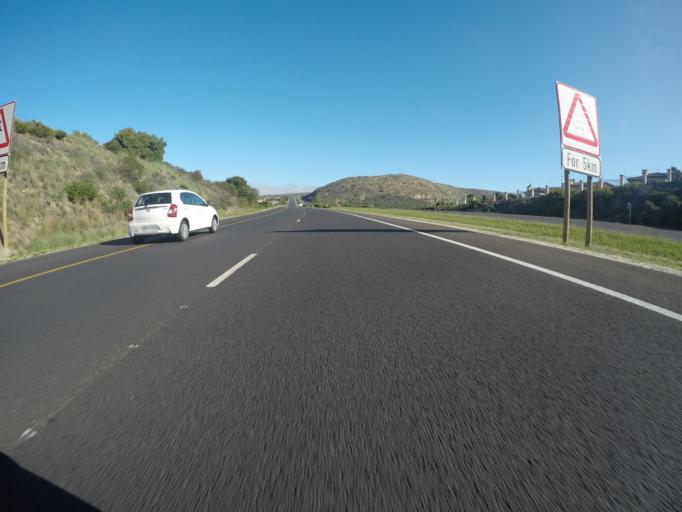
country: ZA
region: Western Cape
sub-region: Eden District Municipality
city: Mossel Bay
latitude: -34.1488
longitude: 22.0987
